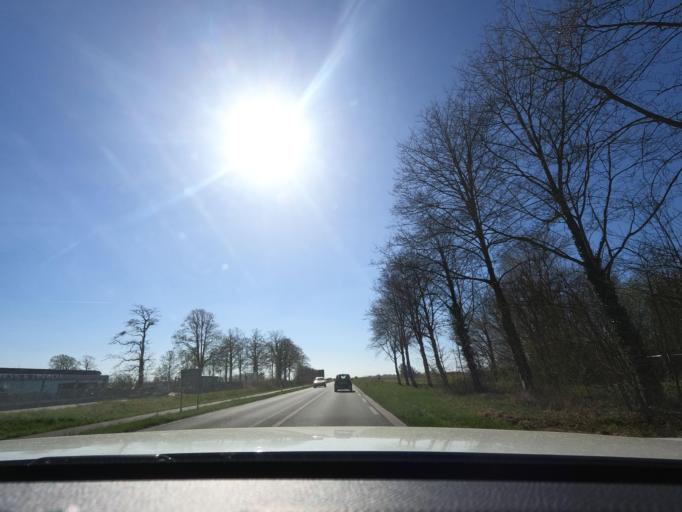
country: NL
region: Gelderland
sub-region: Gemeente Elburg
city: Elburg
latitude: 52.4497
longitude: 5.8270
